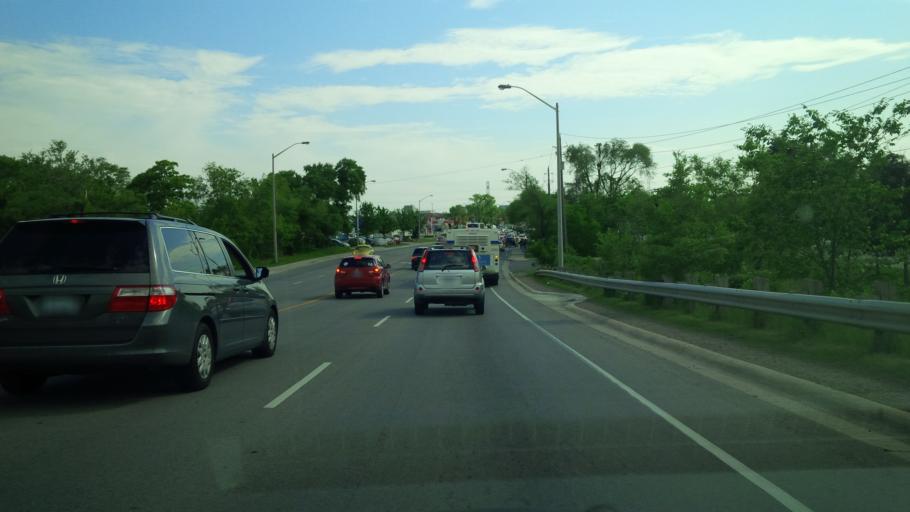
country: CA
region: Ontario
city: Burlington
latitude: 43.3402
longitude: -79.8158
